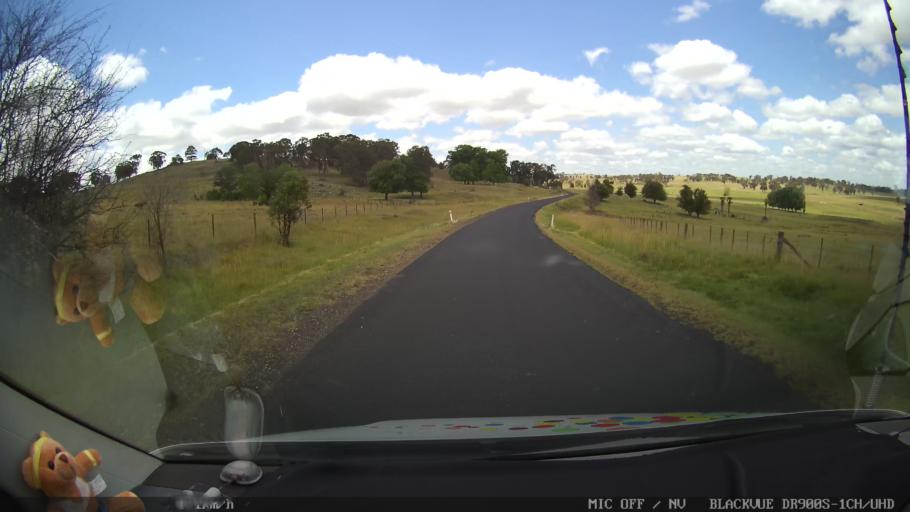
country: AU
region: New South Wales
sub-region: Glen Innes Severn
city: Glen Innes
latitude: -29.4281
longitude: 151.7506
